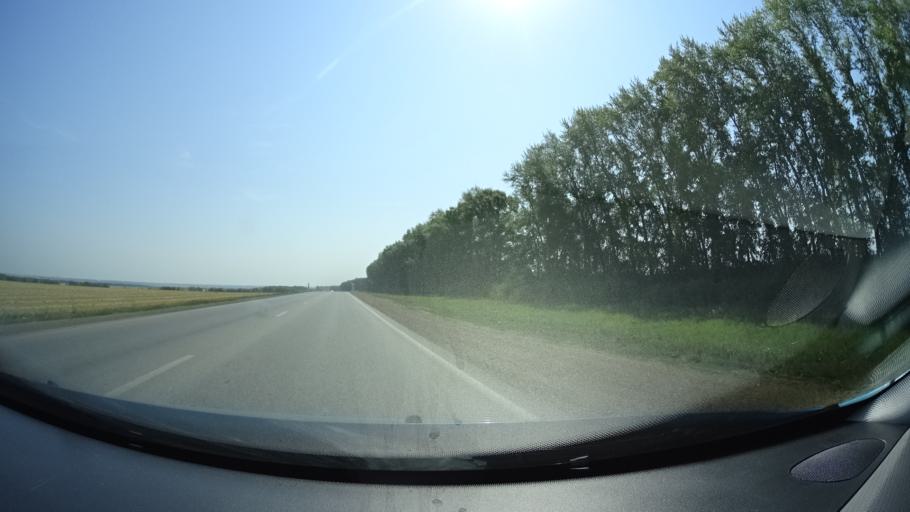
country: RU
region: Bashkortostan
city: Kabakovo
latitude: 54.4722
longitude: 55.9422
